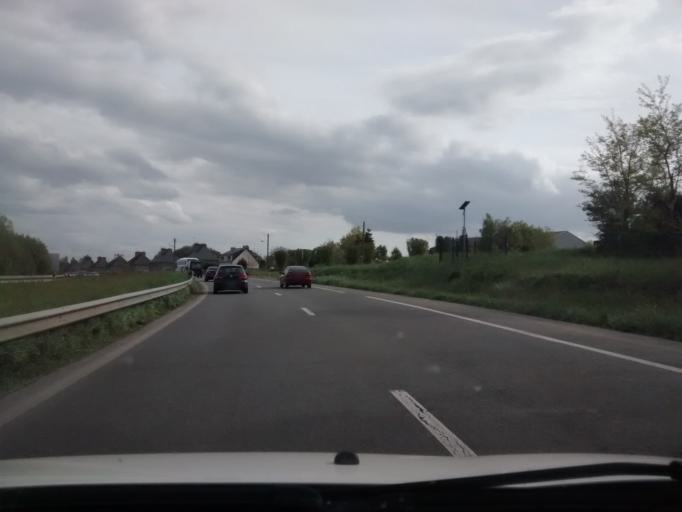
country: FR
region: Brittany
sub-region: Departement d'Ille-et-Vilaine
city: Saint-Pere
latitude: 48.5576
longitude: -1.9292
